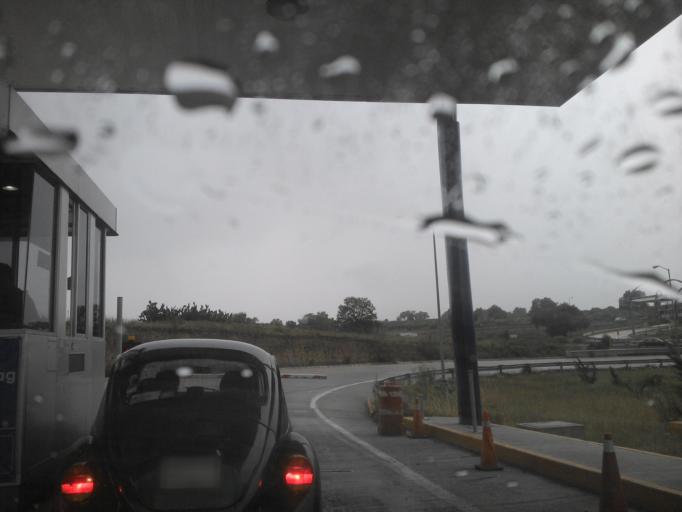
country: MX
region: Morelos
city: Nopaltepec
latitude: 19.8326
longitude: -98.7001
